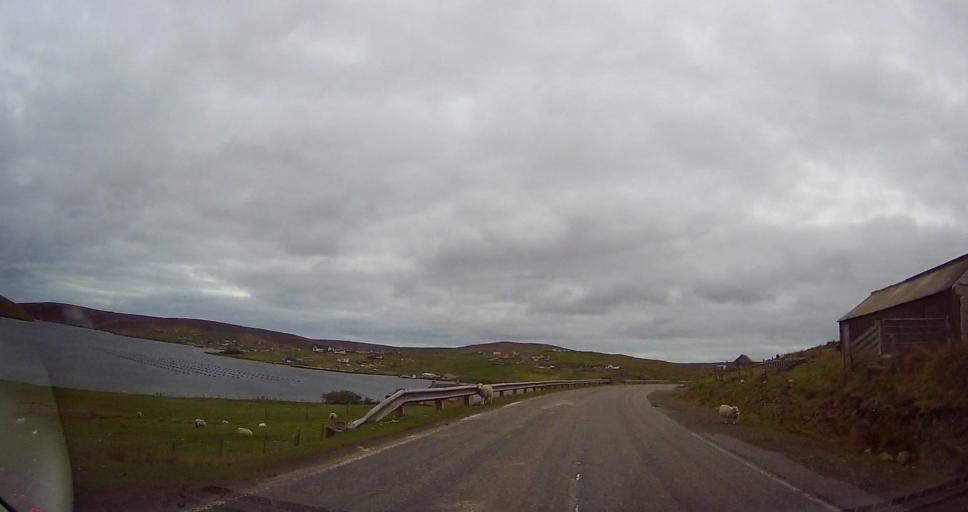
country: GB
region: Scotland
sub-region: Shetland Islands
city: Shetland
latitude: 60.6119
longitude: -1.0736
